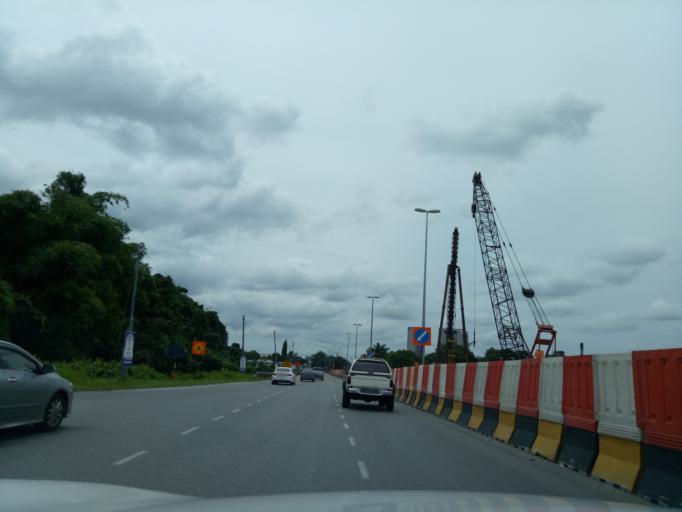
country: MY
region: Sarawak
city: Kuching
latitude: 1.5004
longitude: 110.3324
